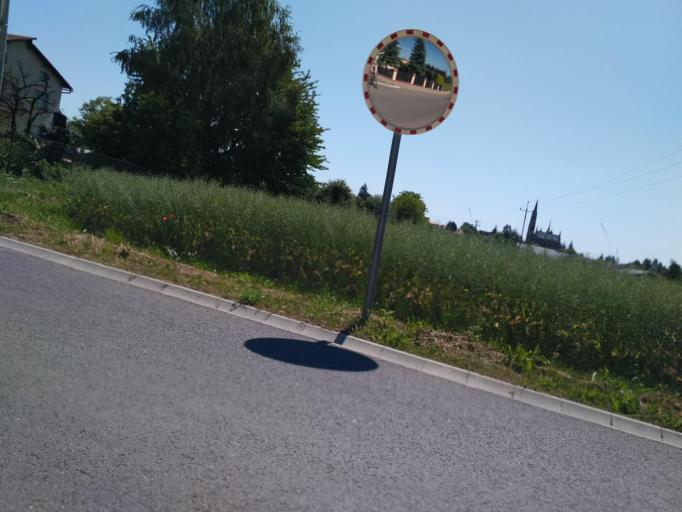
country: PL
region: Subcarpathian Voivodeship
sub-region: Powiat krosnienski
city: Korczyna
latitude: 49.7184
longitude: 21.8028
